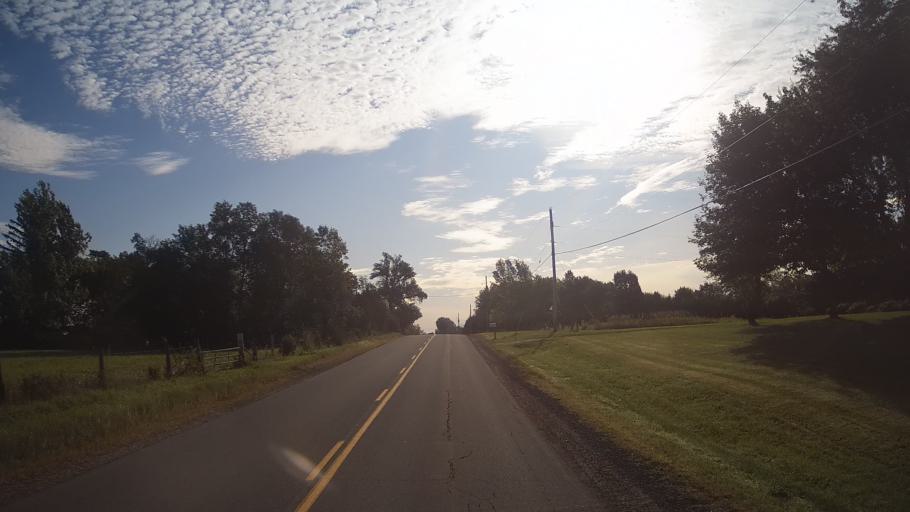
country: CA
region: Ontario
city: Gananoque
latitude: 44.4005
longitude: -76.0885
